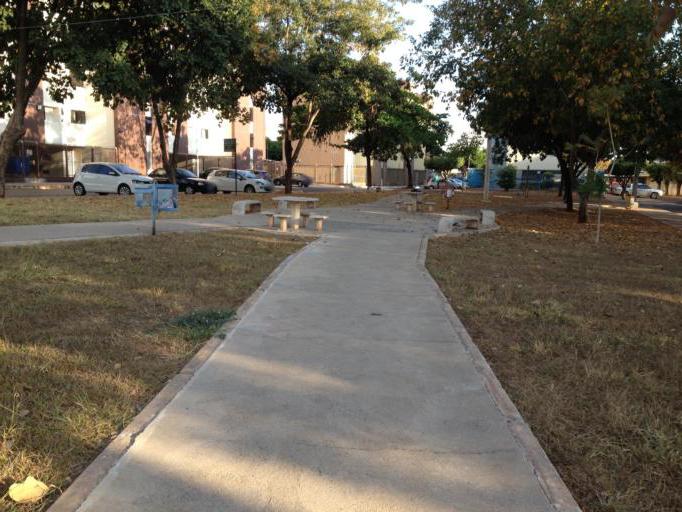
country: BR
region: Federal District
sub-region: Brasilia
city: Brasilia
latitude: -15.7956
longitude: -47.9377
